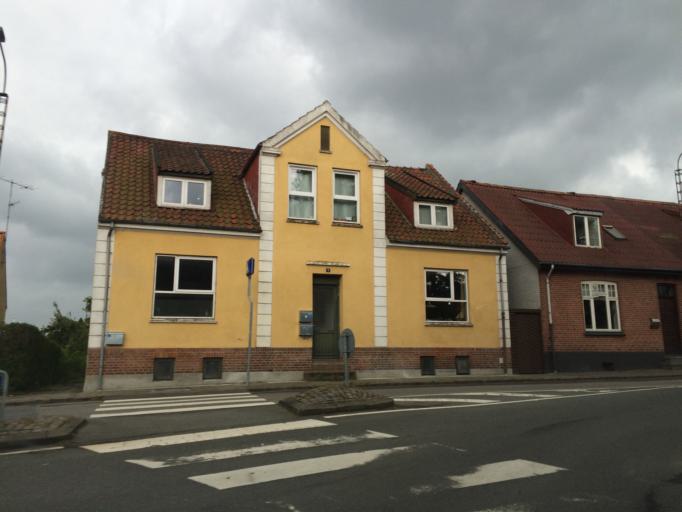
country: DK
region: Central Jutland
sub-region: Silkeborg Kommune
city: Silkeborg
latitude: 56.1636
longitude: 9.5353
